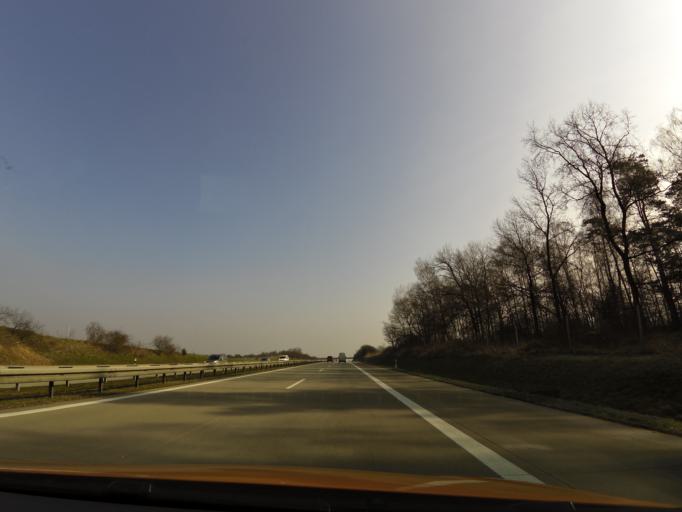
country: DE
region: Brandenburg
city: Jacobsdorf
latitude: 52.3202
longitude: 14.4152
